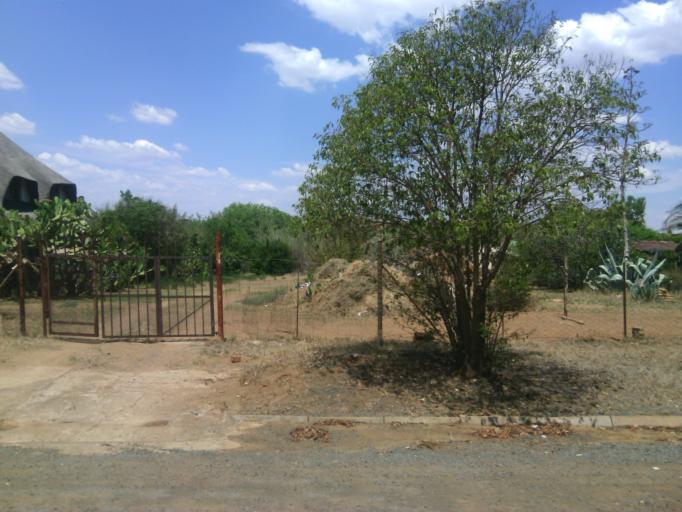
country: ZA
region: Orange Free State
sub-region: Xhariep District Municipality
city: Dewetsdorp
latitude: -29.5777
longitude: 26.6650
